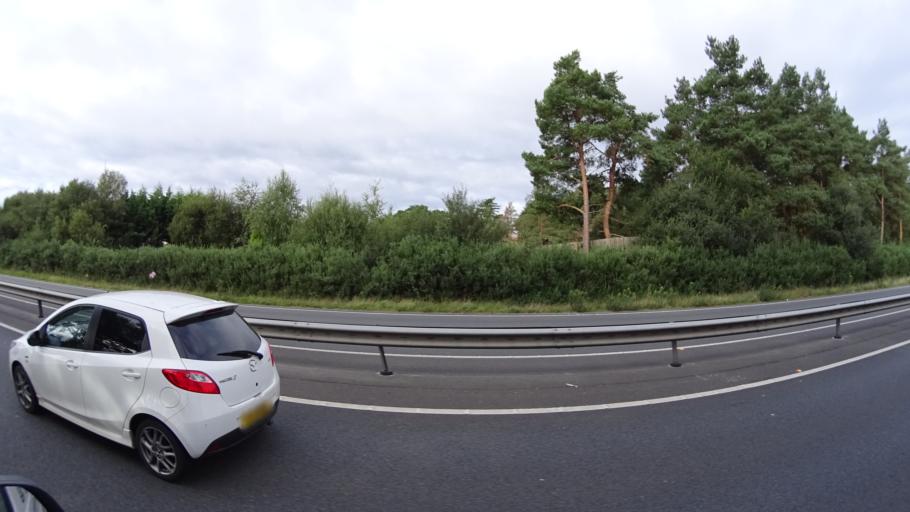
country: GB
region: England
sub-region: Dorset
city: St Leonards
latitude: 50.7966
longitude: -1.8153
